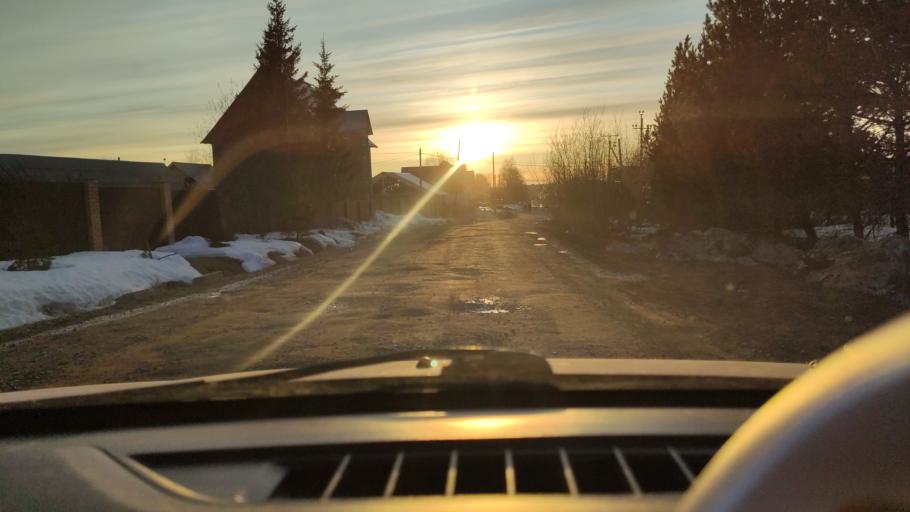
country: RU
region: Perm
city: Polazna
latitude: 58.1161
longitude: 56.4104
